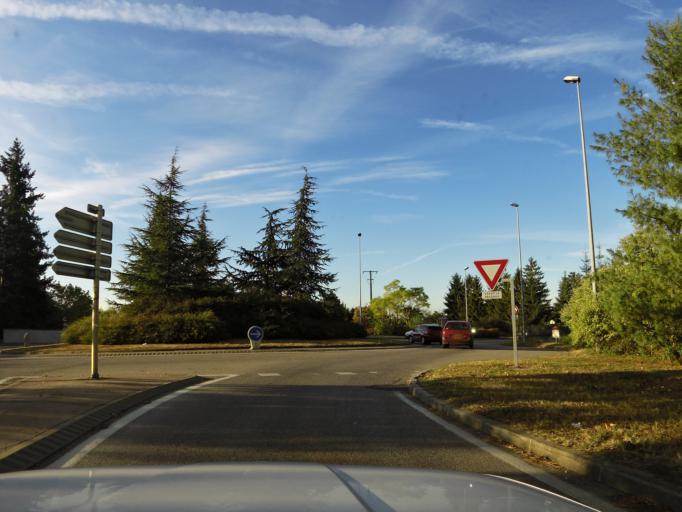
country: FR
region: Rhone-Alpes
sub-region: Departement de l'Ain
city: Saint-Jean-de-Niost
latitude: 45.8514
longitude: 5.2530
